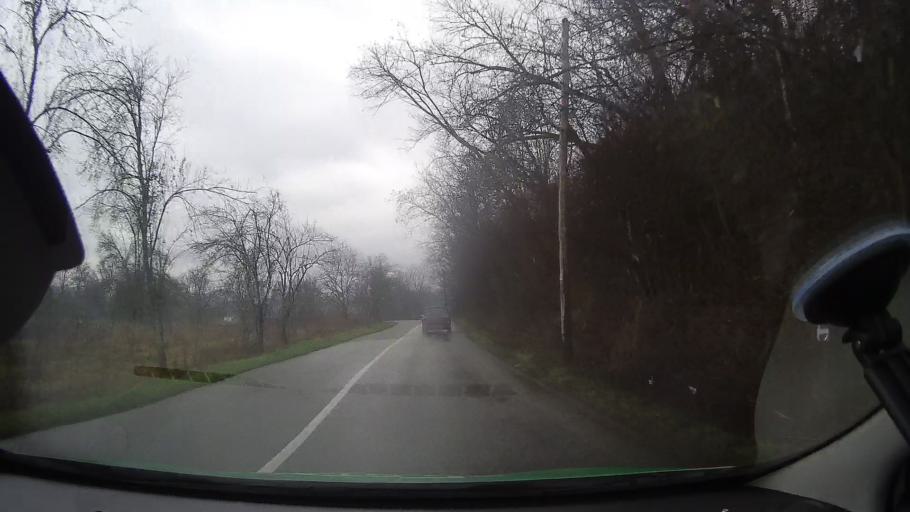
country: RO
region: Arad
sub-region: Comuna Gurahont
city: Gurahont
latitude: 46.2605
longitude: 22.3376
